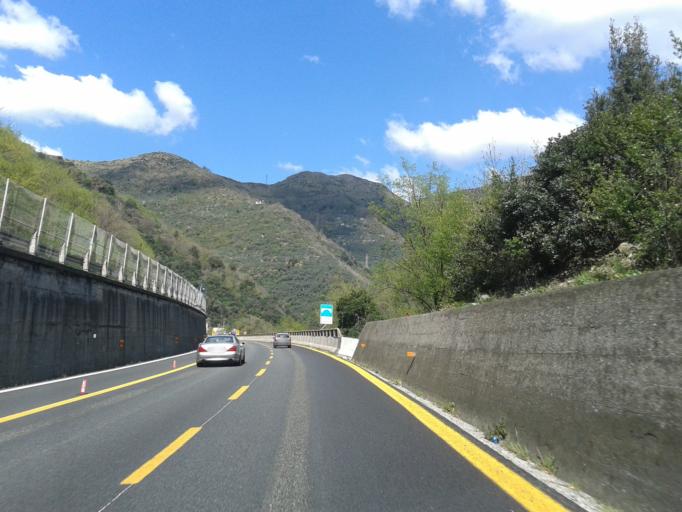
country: IT
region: Liguria
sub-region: Provincia di Genova
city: Sori
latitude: 44.3835
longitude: 9.1027
